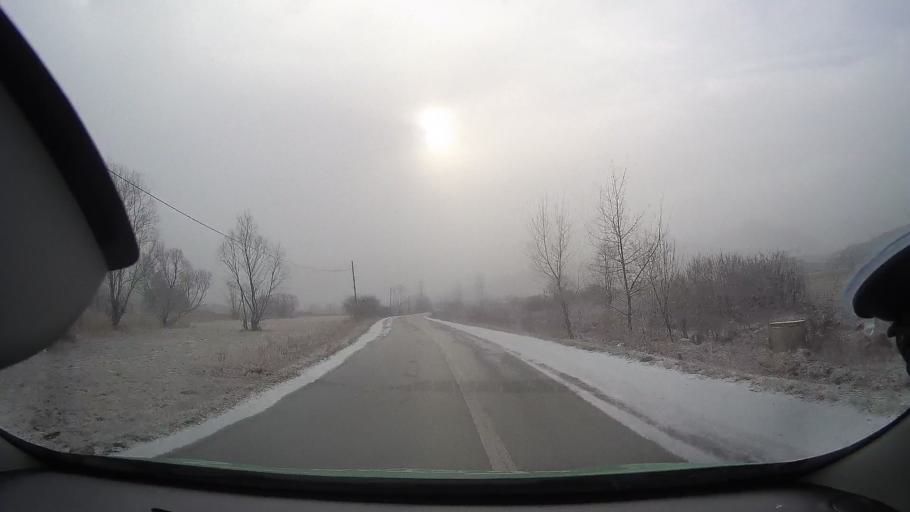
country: RO
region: Alba
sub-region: Comuna Rimetea
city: Rimetea
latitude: 46.4050
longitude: 23.5571
